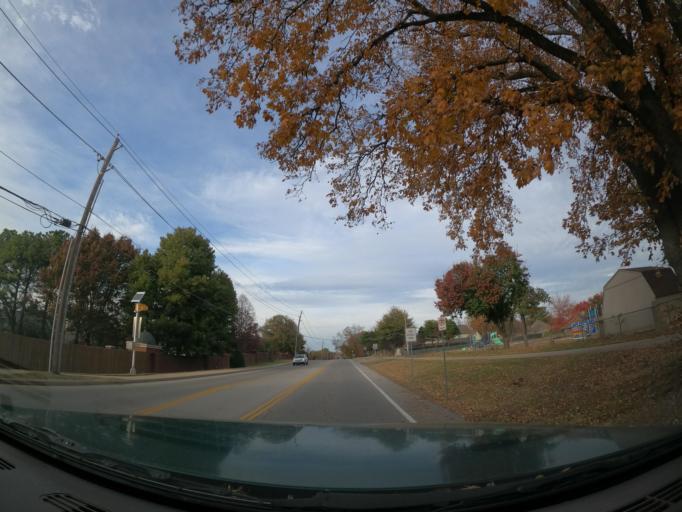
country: US
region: Oklahoma
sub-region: Tulsa County
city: Jenks
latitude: 36.0350
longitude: -95.9400
